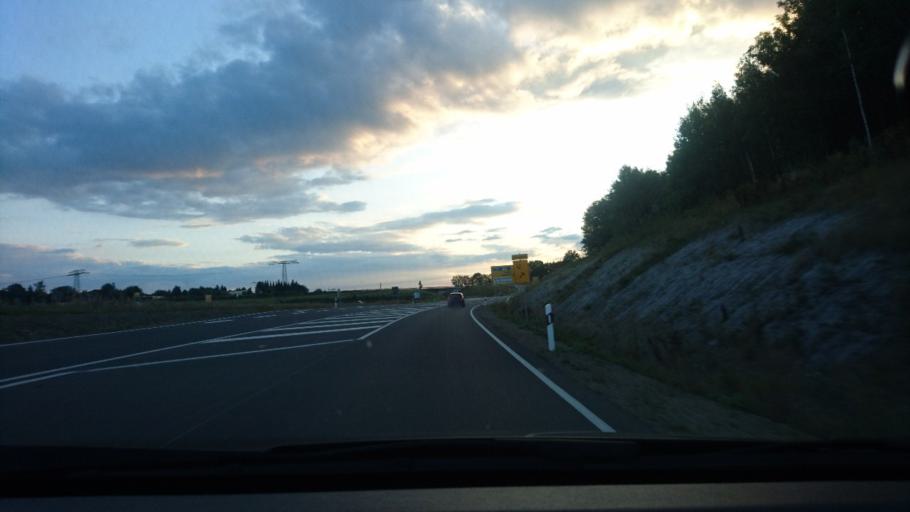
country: DE
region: Saxony
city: Auerbach
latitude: 50.5271
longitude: 12.3847
